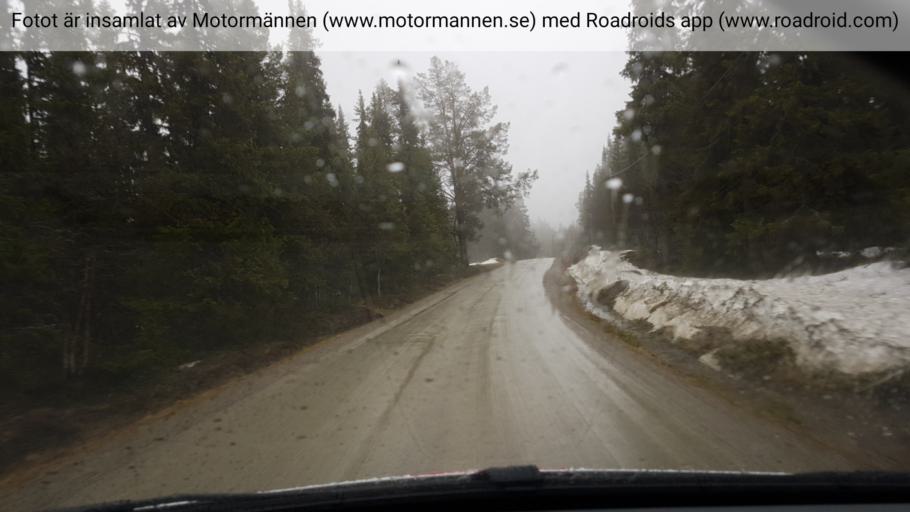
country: SE
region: Jaemtland
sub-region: Are Kommun
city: Jarpen
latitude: 62.6001
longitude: 13.3226
